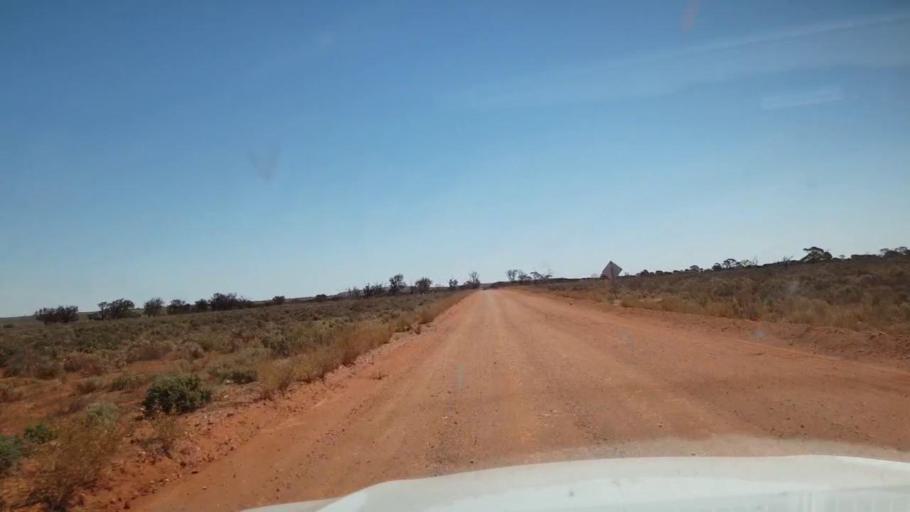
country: AU
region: South Australia
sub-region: Whyalla
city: Whyalla
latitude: -32.6846
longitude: 137.1049
